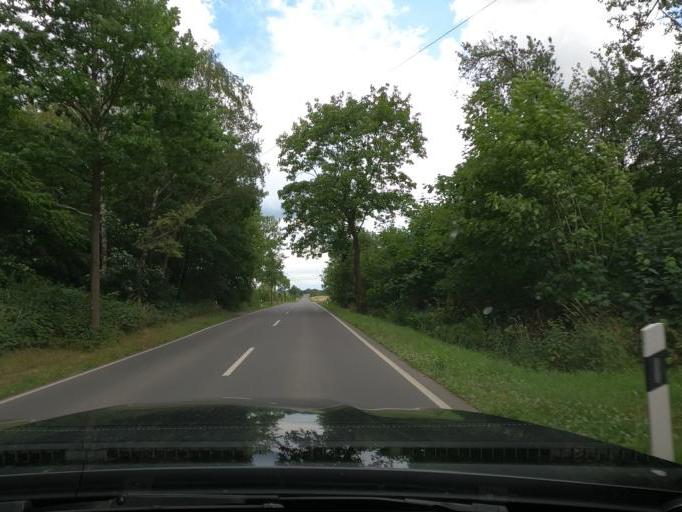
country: DE
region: Lower Saxony
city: Sehnde
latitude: 52.2951
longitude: 9.9954
